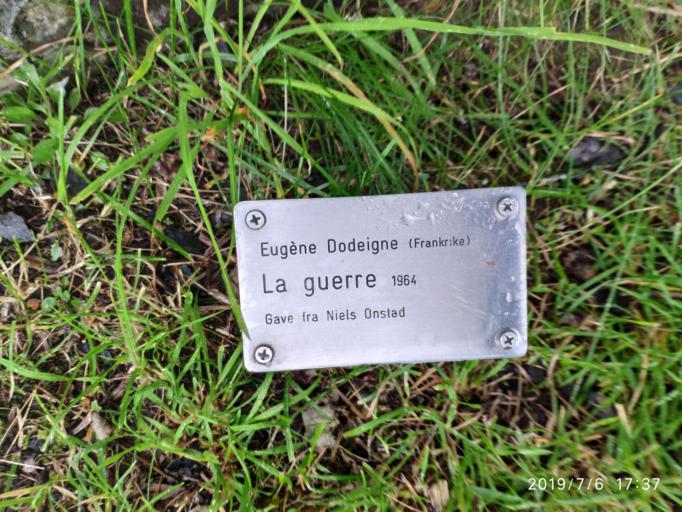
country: NO
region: Akershus
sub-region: Baerum
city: Sandvika
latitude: 59.8892
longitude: 10.5541
